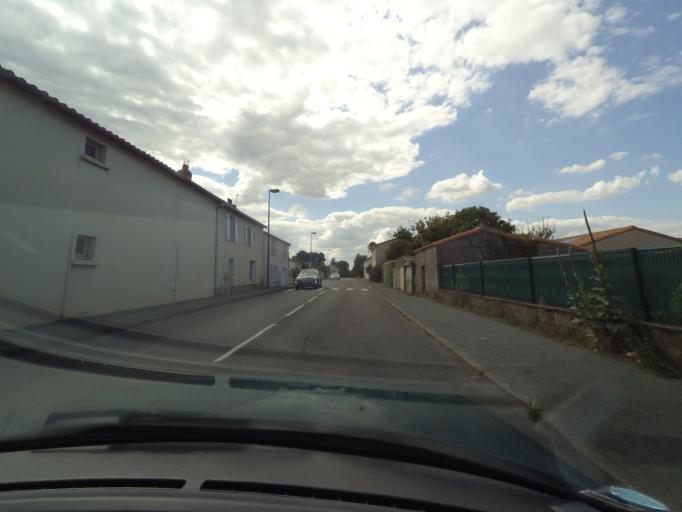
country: FR
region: Pays de la Loire
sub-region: Departement de la Vendee
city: Montaigu
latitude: 46.9746
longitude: -1.3235
